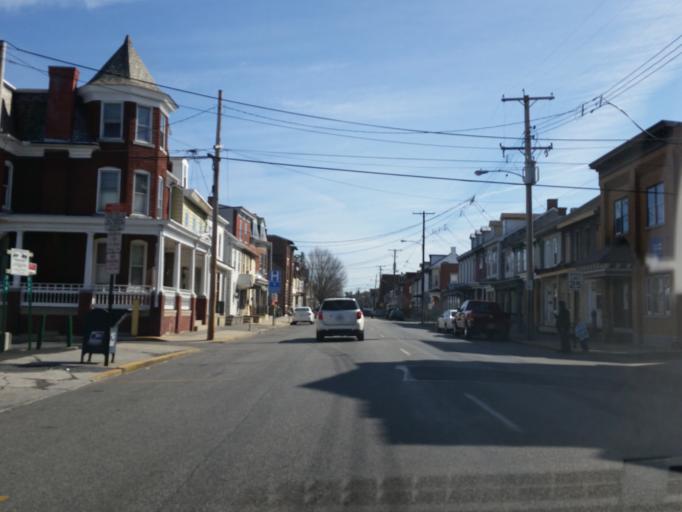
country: US
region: Pennsylvania
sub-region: Lebanon County
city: Lebanon
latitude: 40.3367
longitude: -76.4237
